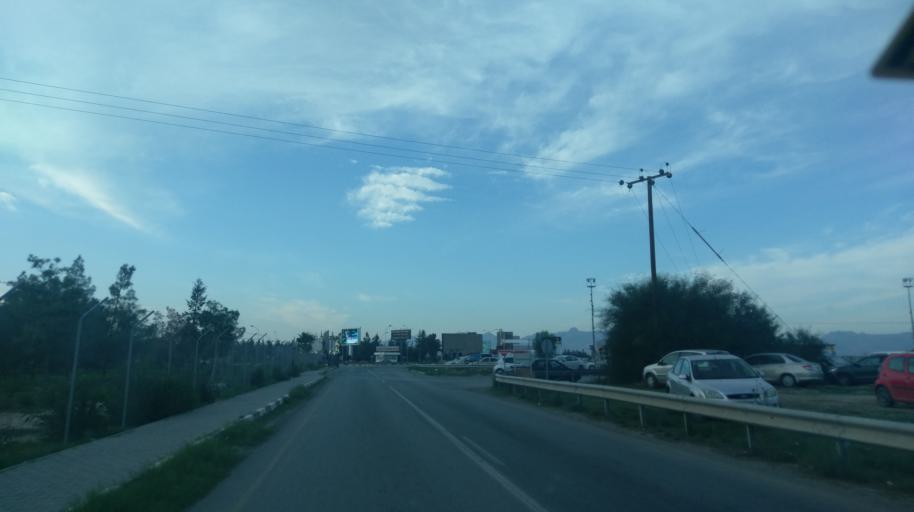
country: CY
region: Lefkosia
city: Geri
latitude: 35.1578
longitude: 33.5063
